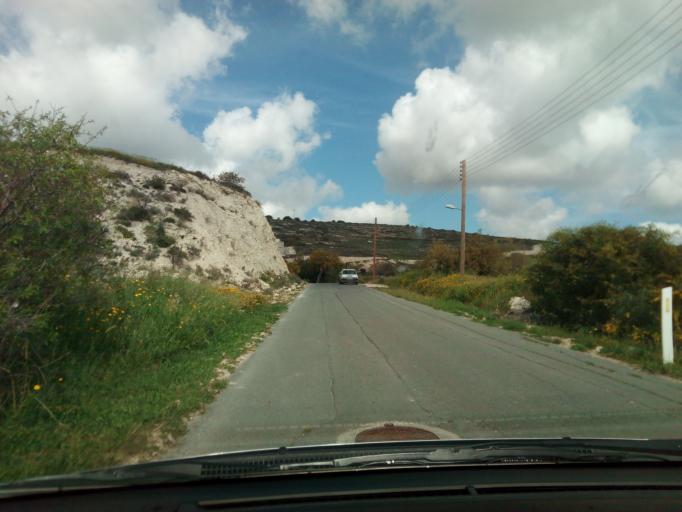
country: CY
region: Pafos
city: Paphos
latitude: 34.7653
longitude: 32.4652
